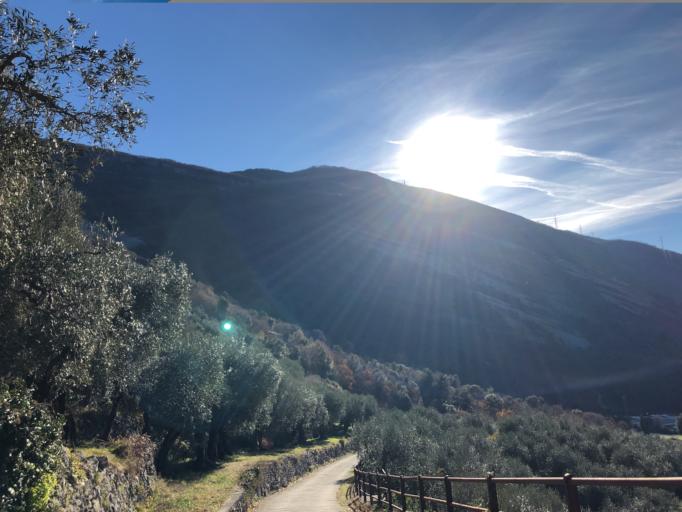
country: IT
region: Trentino-Alto Adige
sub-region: Provincia di Trento
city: Torbole sul Garda
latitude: 45.8675
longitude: 10.8832
